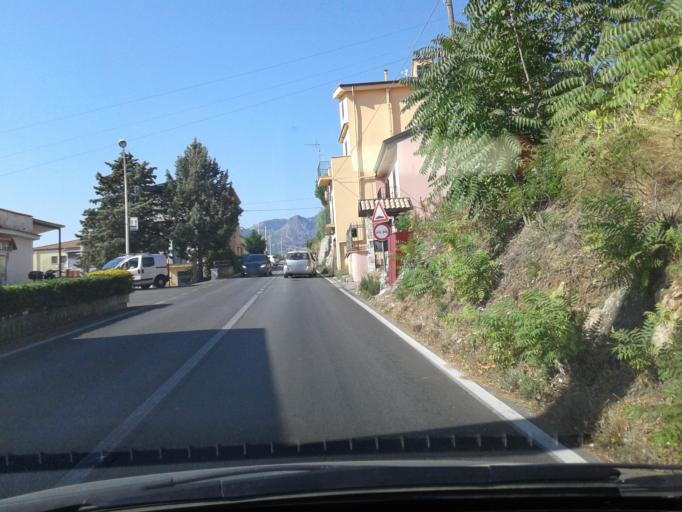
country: IT
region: Sicily
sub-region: Palermo
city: Cannizzaro-Favara
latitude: 38.0648
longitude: 13.2667
